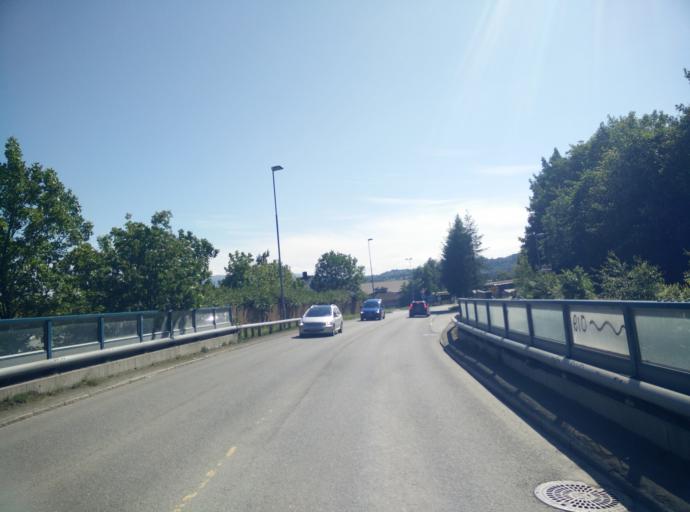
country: NO
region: Sor-Trondelag
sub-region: Trondheim
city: Trondheim
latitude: 63.3992
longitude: 10.3581
